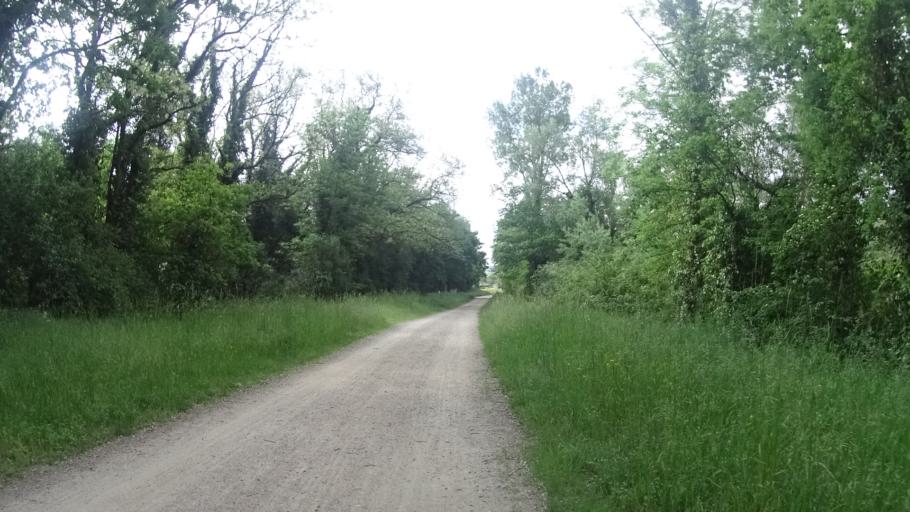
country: DE
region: Baden-Wuerttemberg
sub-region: Freiburg Region
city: Bad Bellingen
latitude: 47.7384
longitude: 7.5499
